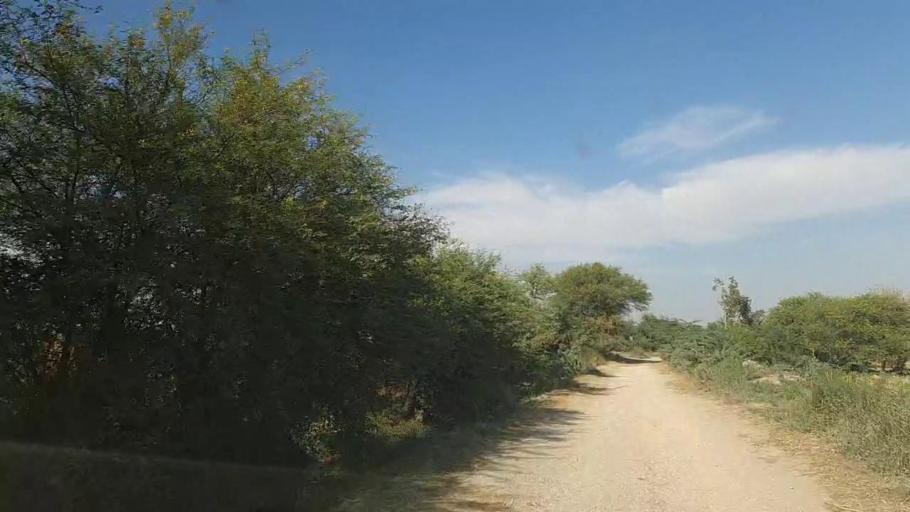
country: PK
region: Sindh
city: Bulri
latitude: 24.8607
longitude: 68.2600
